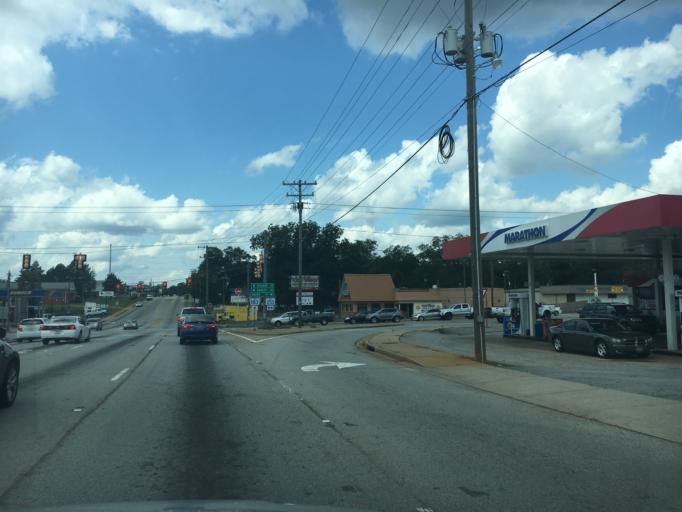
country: US
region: South Carolina
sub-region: Greenville County
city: Sans Souci
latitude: 34.8709
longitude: -82.4291
